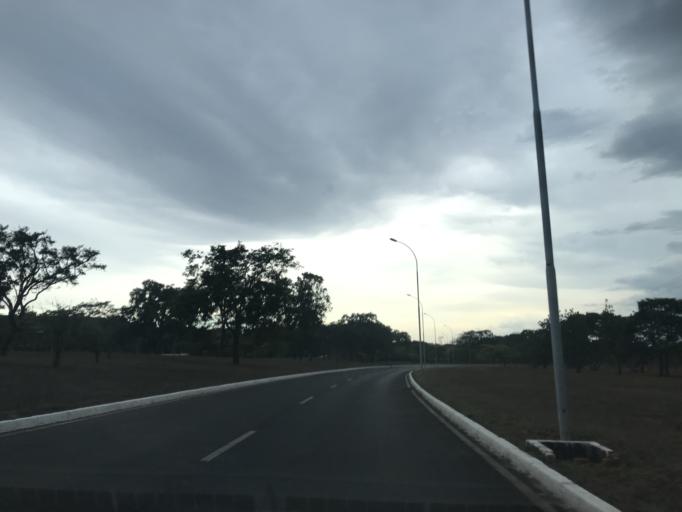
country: BR
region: Federal District
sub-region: Brasilia
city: Brasilia
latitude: -15.8376
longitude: -47.9270
